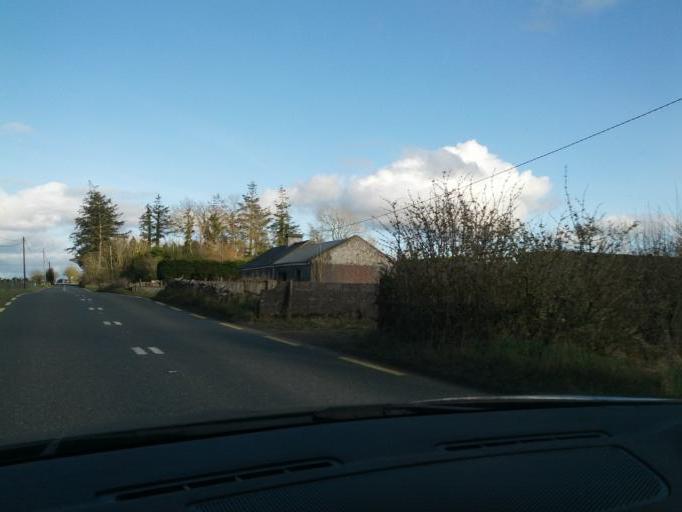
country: IE
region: Connaught
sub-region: Roscommon
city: Roscommon
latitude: 53.6519
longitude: -8.2455
